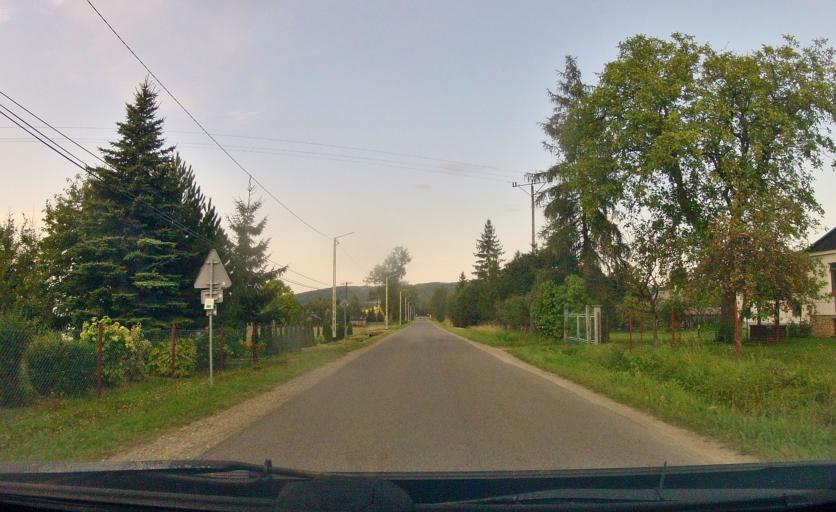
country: PL
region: Subcarpathian Voivodeship
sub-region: Powiat krosnienski
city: Dukla
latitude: 49.5552
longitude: 21.6244
